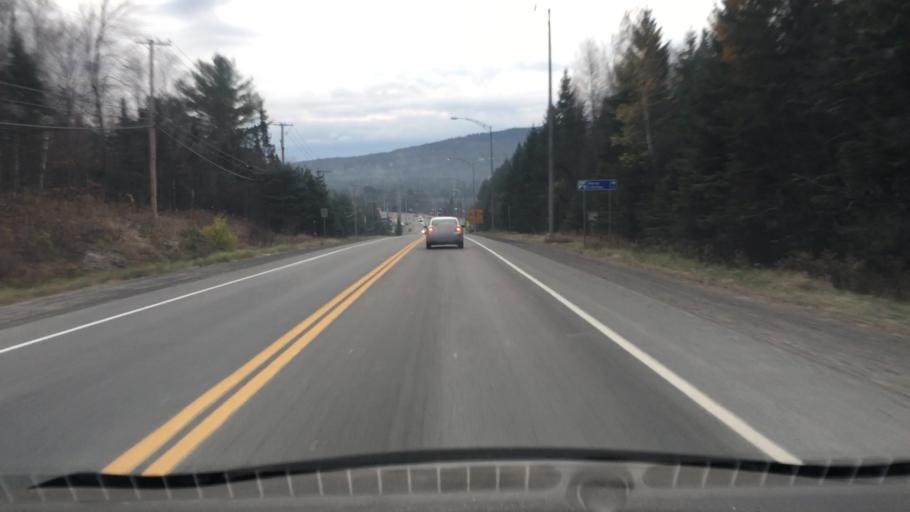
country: CA
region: Quebec
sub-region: Laurentides
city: Saint-Sauveur
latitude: 45.9058
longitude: -74.2501
